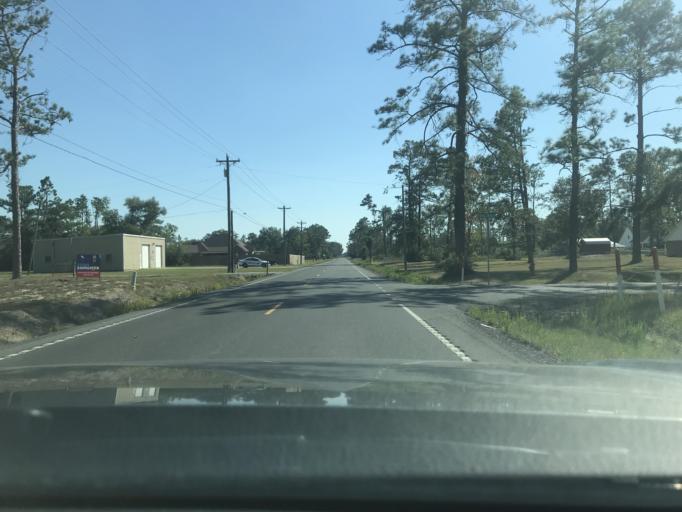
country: US
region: Louisiana
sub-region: Calcasieu Parish
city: Moss Bluff
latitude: 30.3292
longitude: -93.2581
